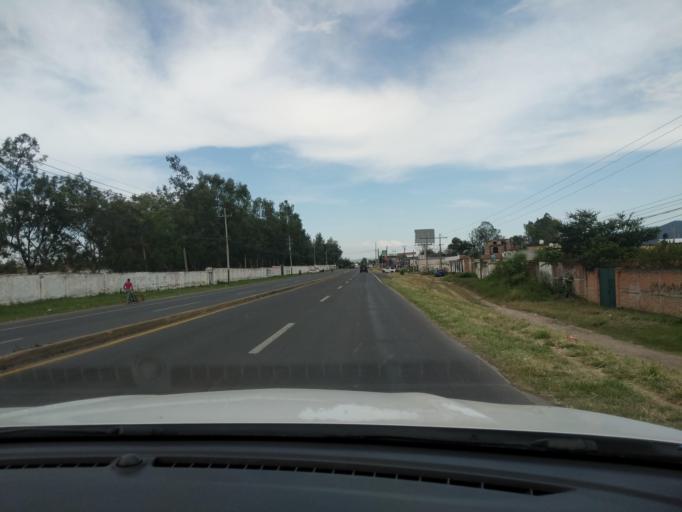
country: MX
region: Jalisco
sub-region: El Salto
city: Galaxia Bonito Jalisco
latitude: 20.5110
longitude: -103.1954
